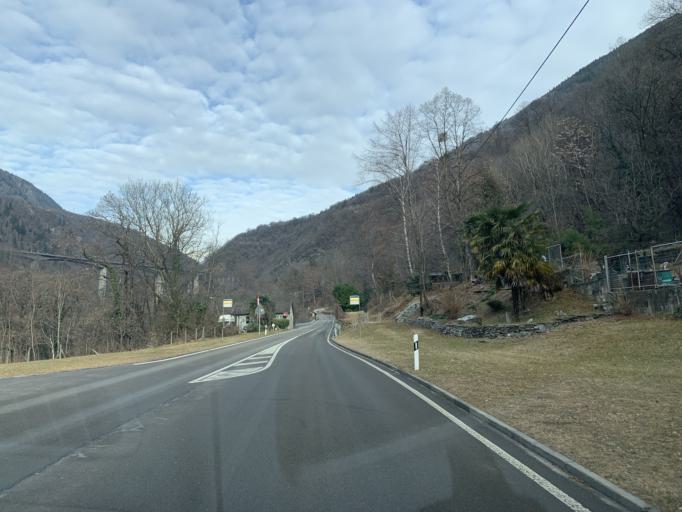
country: CH
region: Ticino
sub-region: Blenio District
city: Cancori
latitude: 46.4143
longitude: 8.8661
